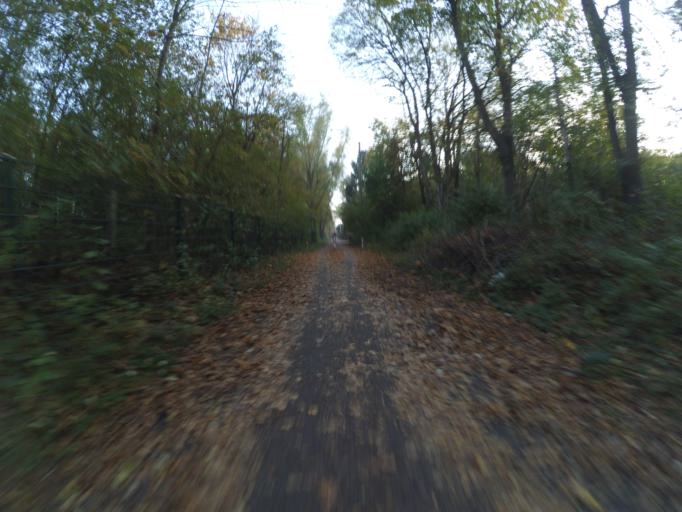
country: DE
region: Bavaria
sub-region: Upper Bavaria
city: Oberschleissheim
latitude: 48.1982
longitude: 11.5399
